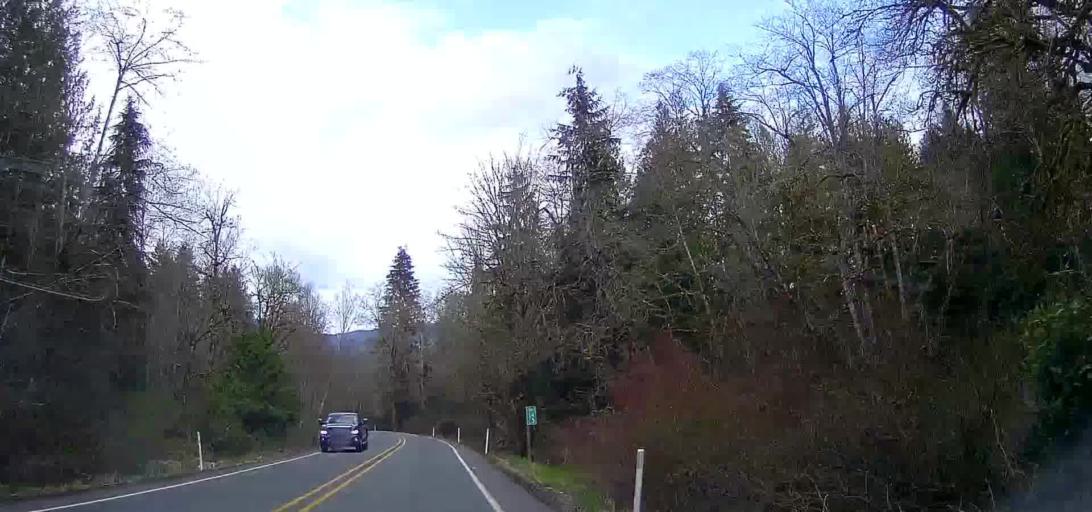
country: US
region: Washington
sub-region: Skagit County
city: Big Lake
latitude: 48.3456
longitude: -122.2046
